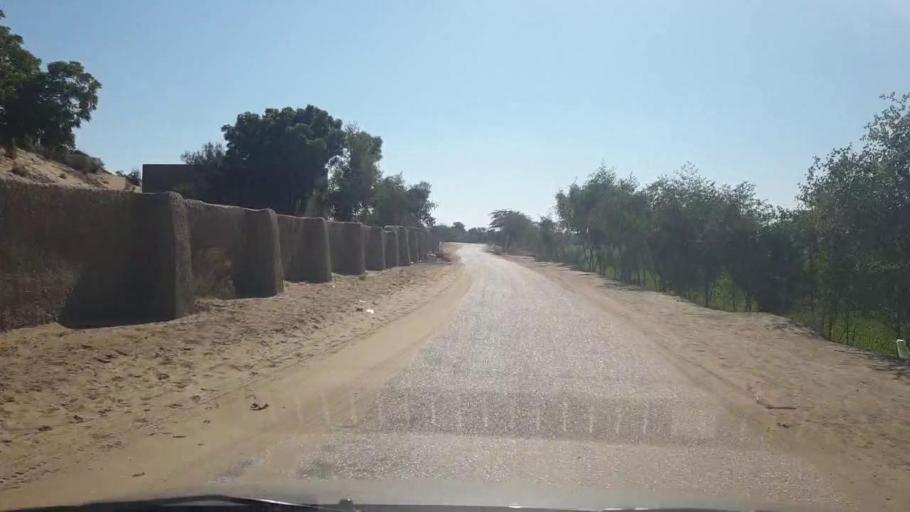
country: PK
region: Sindh
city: Bozdar
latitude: 27.0539
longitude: 68.6481
